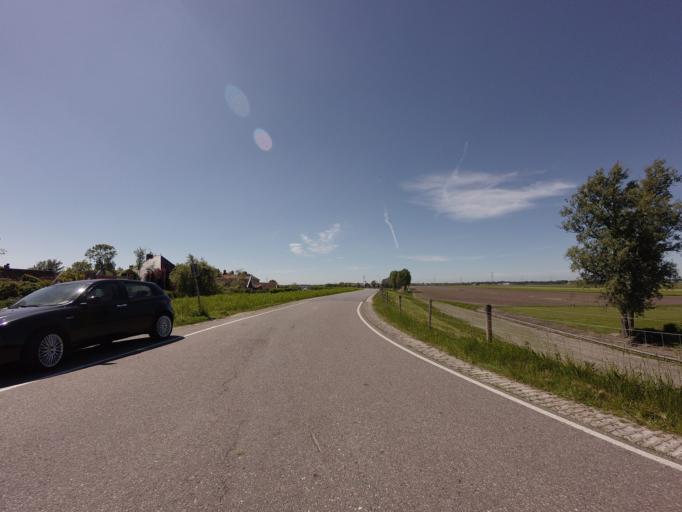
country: NL
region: North Holland
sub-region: Gemeente Alkmaar
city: Alkmaar
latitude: 52.5786
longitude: 4.8067
